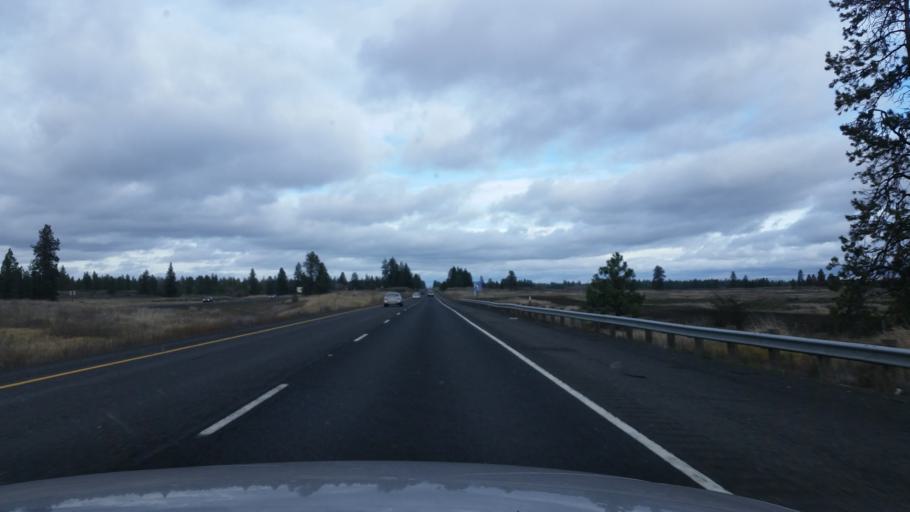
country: US
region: Washington
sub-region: Spokane County
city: Medical Lake
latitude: 47.4051
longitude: -117.8284
